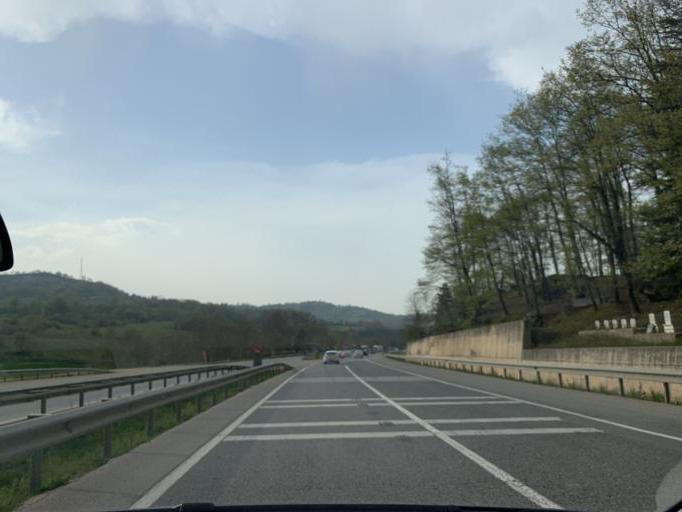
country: TR
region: Bursa
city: Tahtakopru
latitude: 39.9614
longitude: 29.6572
